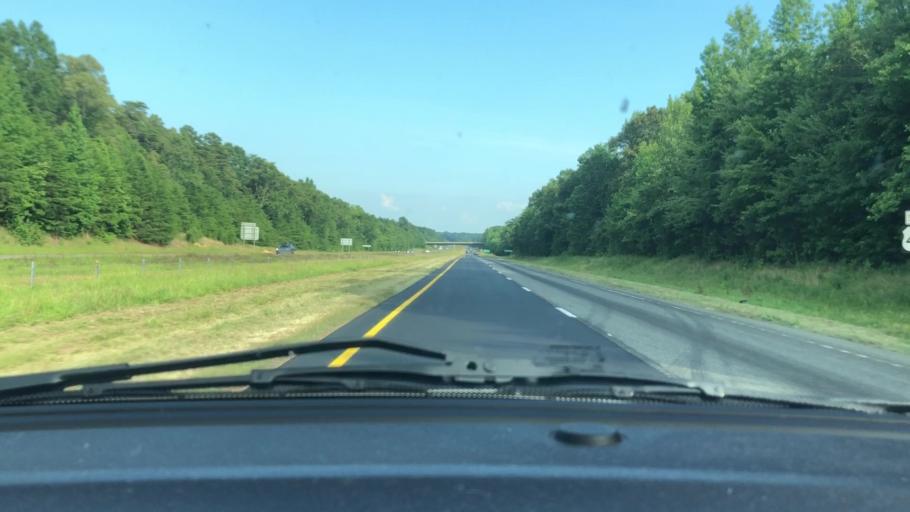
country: US
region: North Carolina
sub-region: Randolph County
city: Liberty
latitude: 35.8082
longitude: -79.5461
